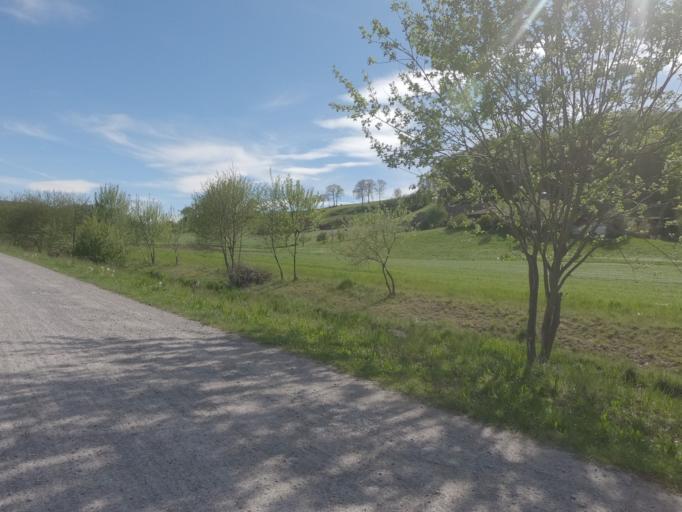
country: CH
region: Bern
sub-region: Bern-Mittelland District
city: Vechigen
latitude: 46.9374
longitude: 7.5517
